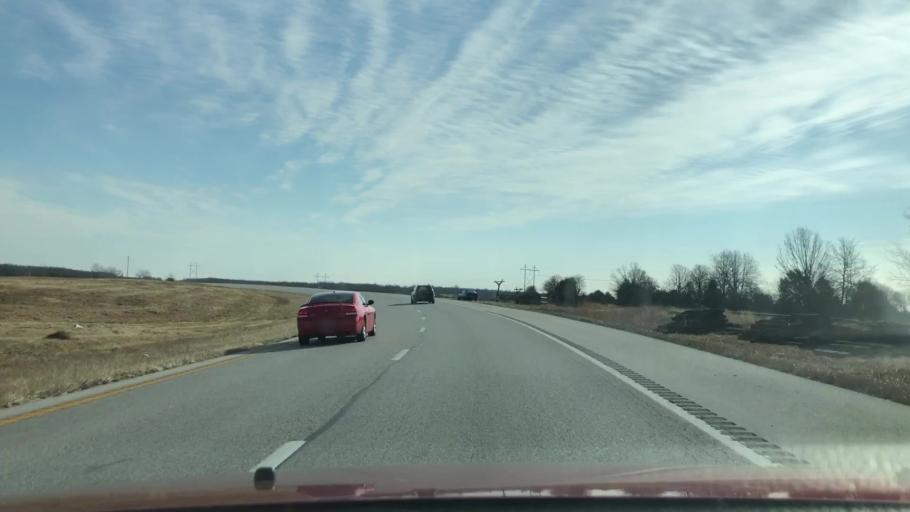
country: US
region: Missouri
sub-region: Webster County
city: Seymour
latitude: 37.1190
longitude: -92.6948
